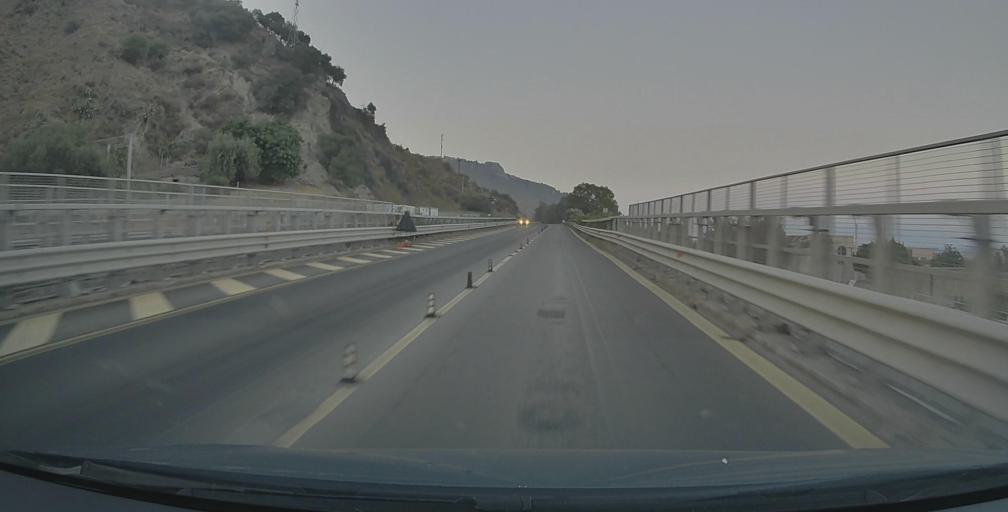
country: IT
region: Sicily
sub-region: Messina
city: Letojanni
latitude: 37.8926
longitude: 15.3200
